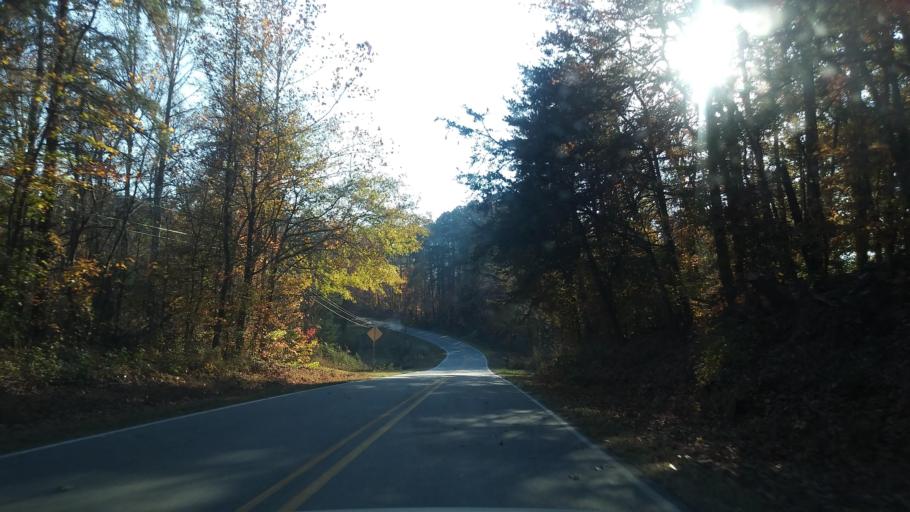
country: US
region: North Carolina
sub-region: Rockingham County
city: Reidsville
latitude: 36.2336
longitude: -79.7180
